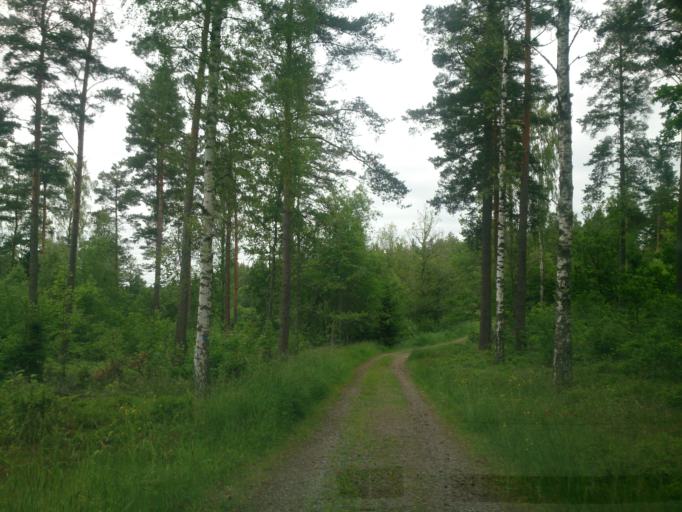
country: SE
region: OEstergoetland
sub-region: Atvidabergs Kommun
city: Atvidaberg
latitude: 58.2091
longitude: 15.9997
